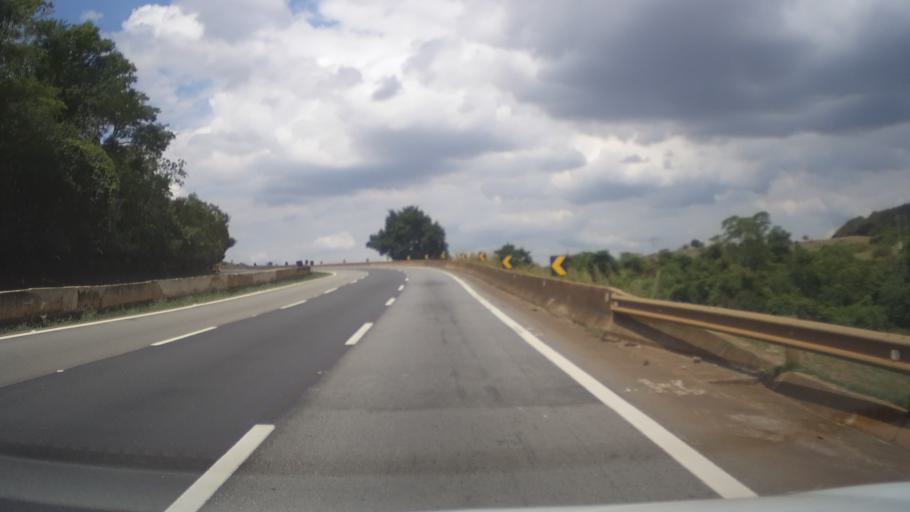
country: BR
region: Minas Gerais
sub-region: Nepomuceno
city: Nepomuceno
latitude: -21.2874
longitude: -45.1434
